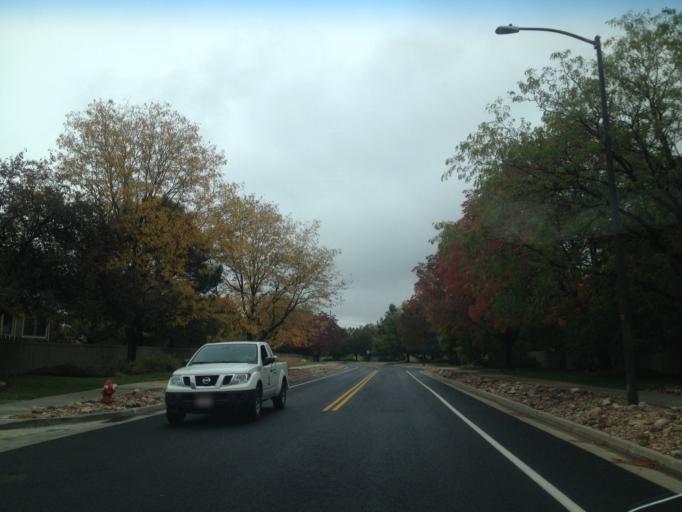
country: US
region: Colorado
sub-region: Boulder County
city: Superior
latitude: 39.9777
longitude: -105.1600
